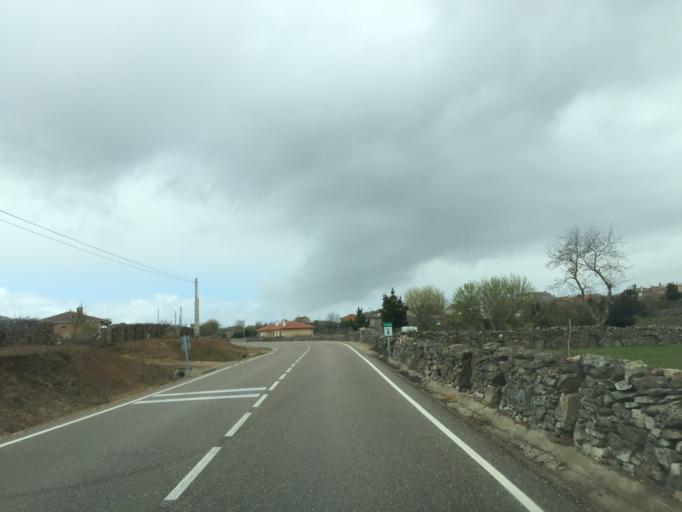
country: ES
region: Castille and Leon
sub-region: Provincia de Zamora
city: Villalcampo
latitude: 41.5231
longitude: -6.0426
